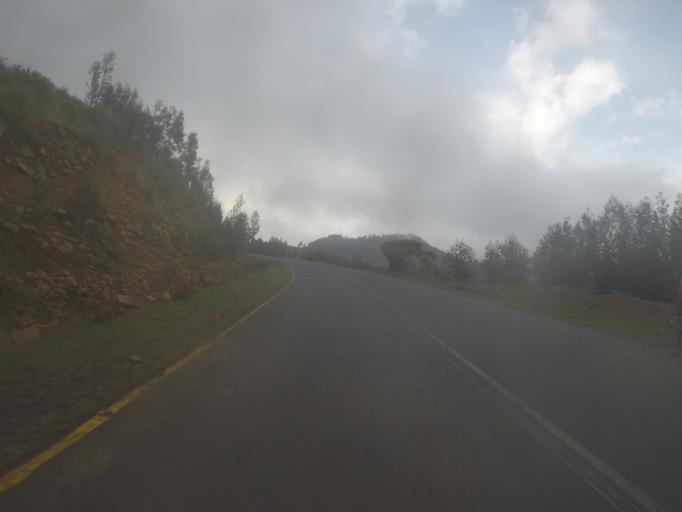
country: ET
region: Amhara
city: Gondar
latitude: 12.7228
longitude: 37.5045
